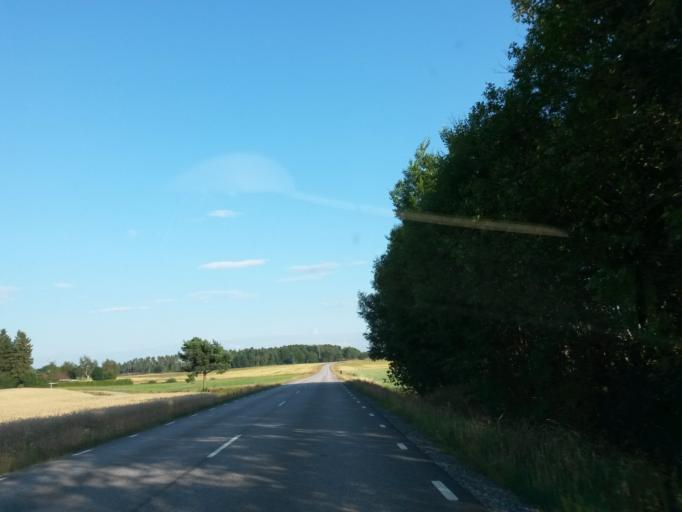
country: SE
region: Vaestra Goetaland
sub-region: Vargarda Kommun
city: Vargarda
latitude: 58.1499
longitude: 12.8560
